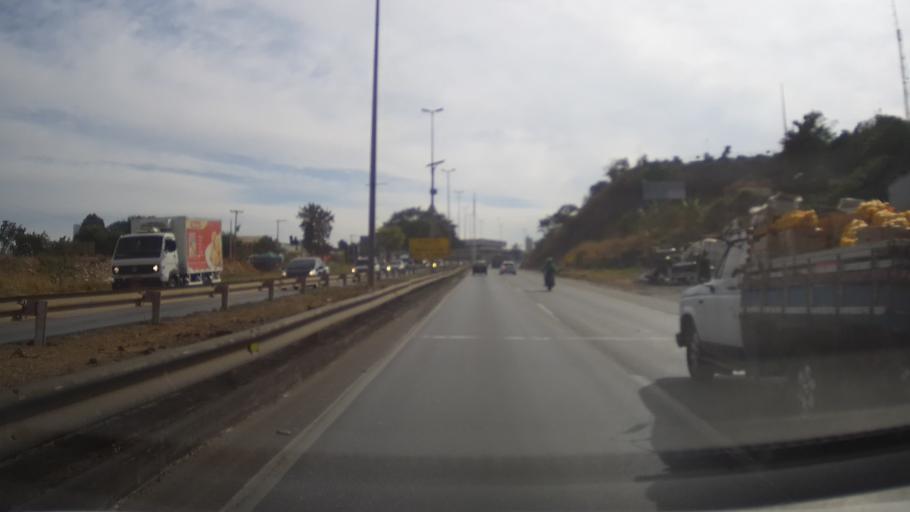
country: BR
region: Minas Gerais
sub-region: Contagem
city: Contagem
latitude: -19.9199
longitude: -44.0320
